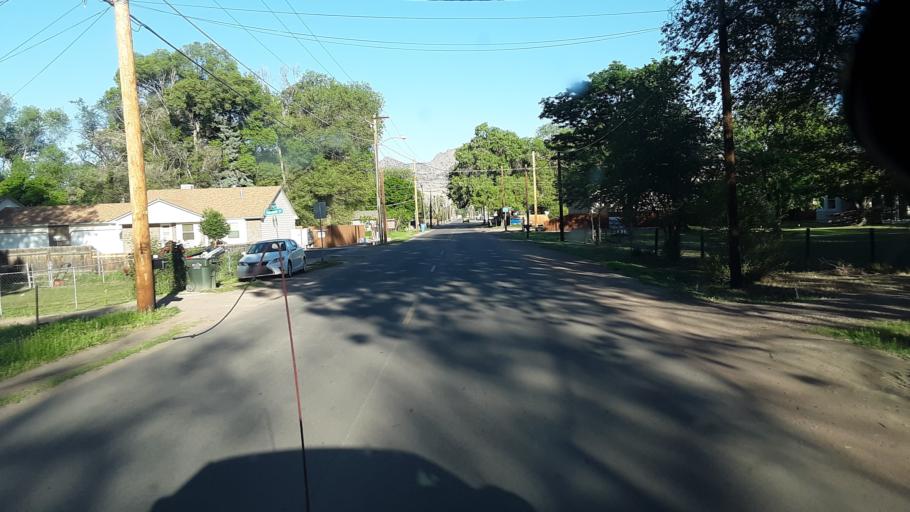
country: US
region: Colorado
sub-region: Fremont County
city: Lincoln Park
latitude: 38.4467
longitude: -105.2162
